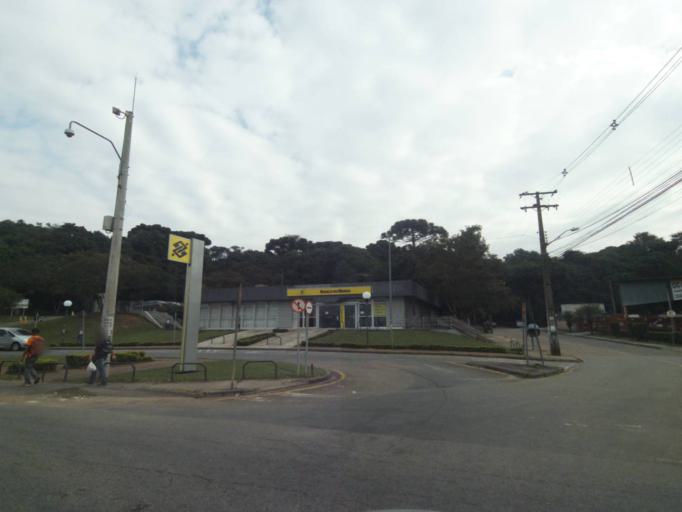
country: BR
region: Parana
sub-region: Curitiba
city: Curitiba
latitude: -25.5141
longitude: -49.3180
